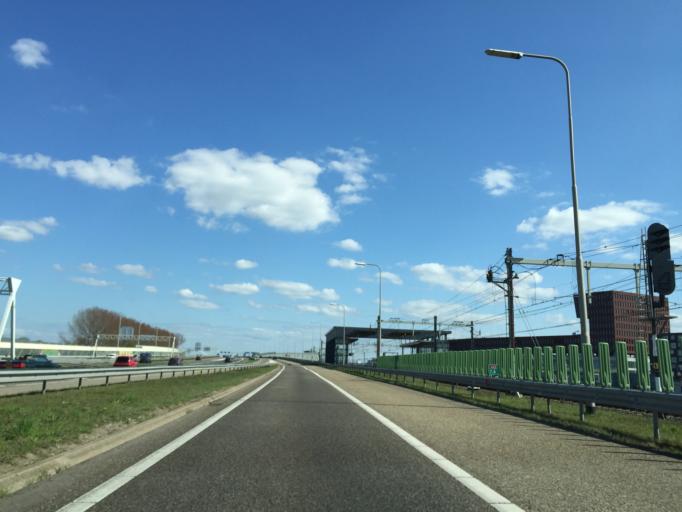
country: NL
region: South Holland
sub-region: Gemeente Den Haag
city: Ypenburg
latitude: 52.0569
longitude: 4.3880
